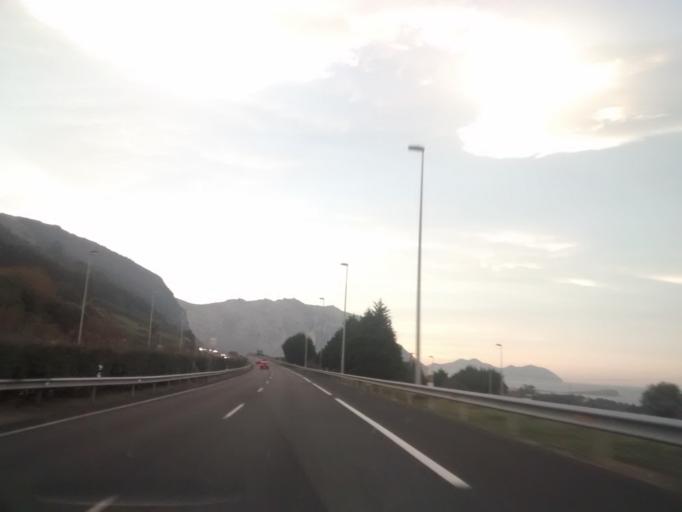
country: ES
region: Cantabria
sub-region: Provincia de Cantabria
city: Castro-Urdiales
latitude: 43.4024
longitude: -3.2907
